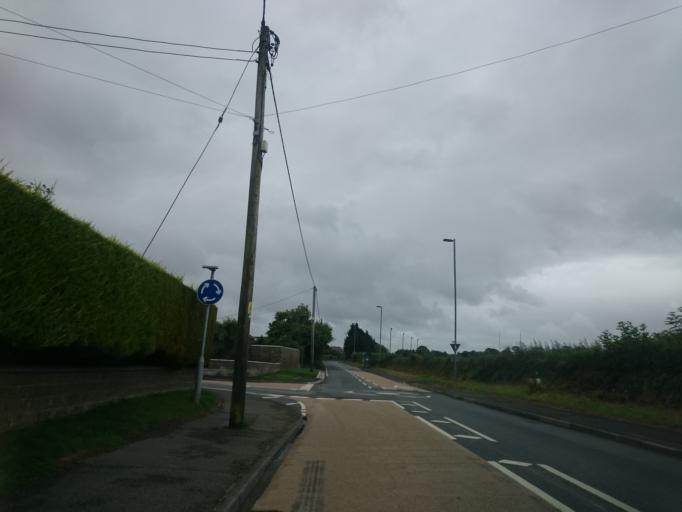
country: GB
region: Wales
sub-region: Pembrokeshire
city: Haverfordwest
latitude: 51.7858
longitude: -4.9744
